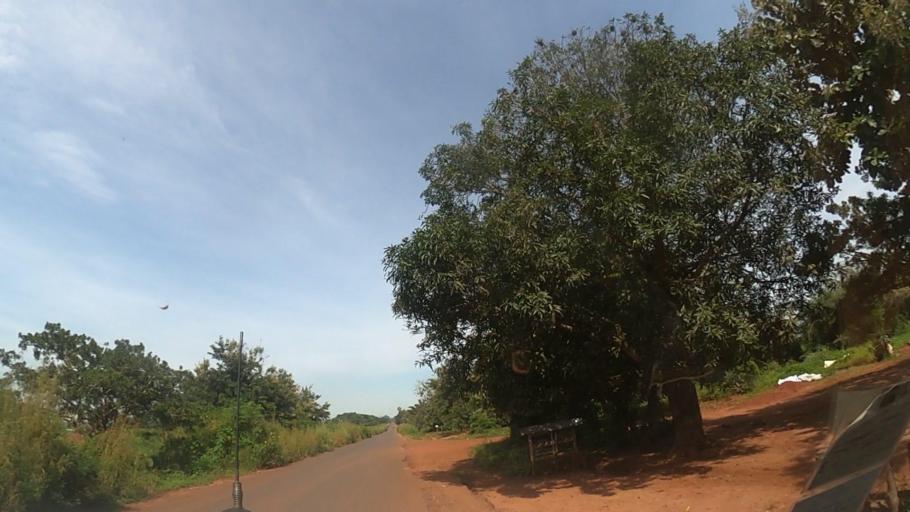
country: CF
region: Ombella-Mpoko
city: Bimbo
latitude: 4.3146
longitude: 18.4693
